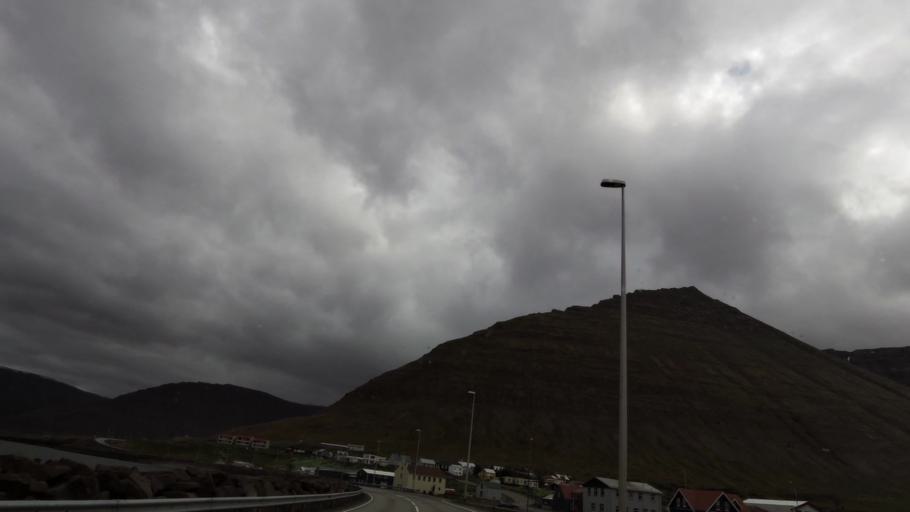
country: IS
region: Westfjords
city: Isafjoerdur
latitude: 66.1126
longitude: -23.1213
